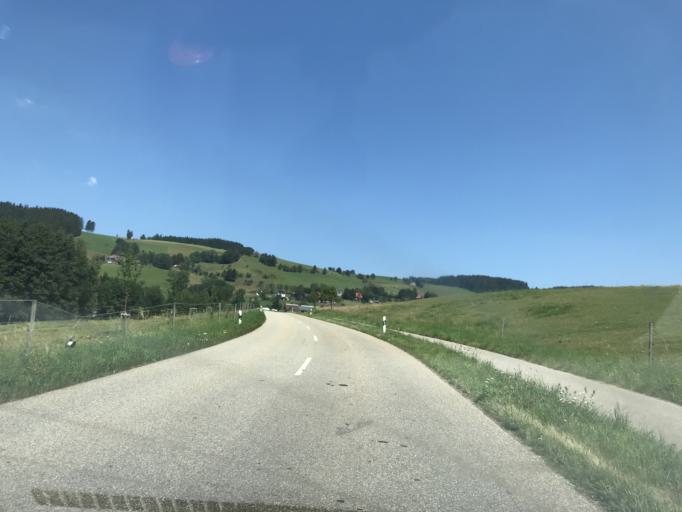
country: DE
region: Baden-Wuerttemberg
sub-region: Freiburg Region
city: Sankt Peter
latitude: 48.0171
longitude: 8.0418
